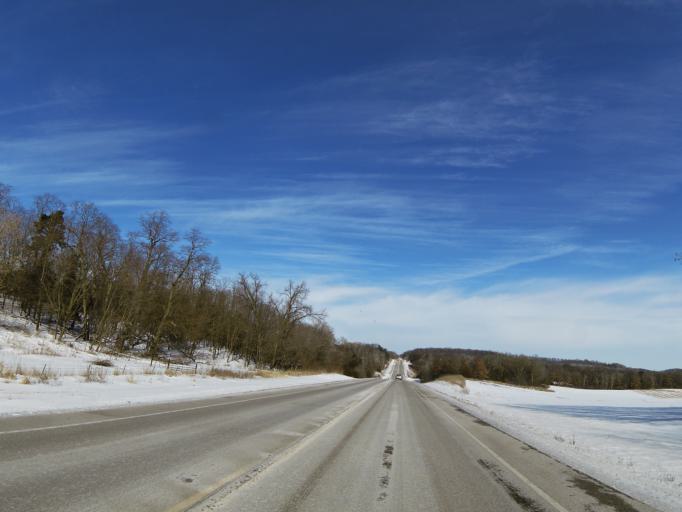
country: US
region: Minnesota
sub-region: Washington County
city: Afton
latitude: 44.8662
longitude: -92.7311
